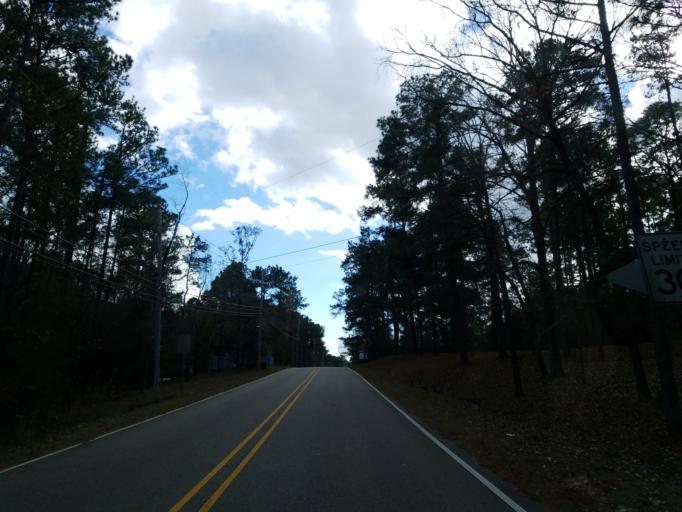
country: US
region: Mississippi
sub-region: Lamar County
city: West Hattiesburg
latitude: 31.2922
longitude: -89.3479
